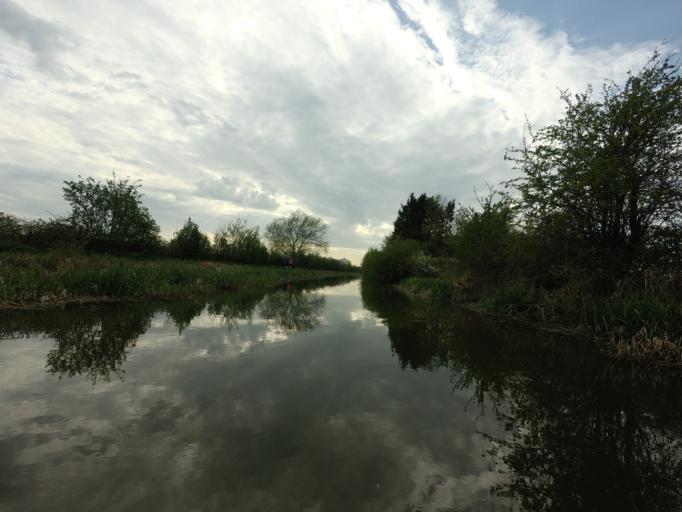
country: GB
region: England
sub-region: Buckinghamshire
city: Aston Clinton
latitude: 51.8166
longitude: -0.7208
